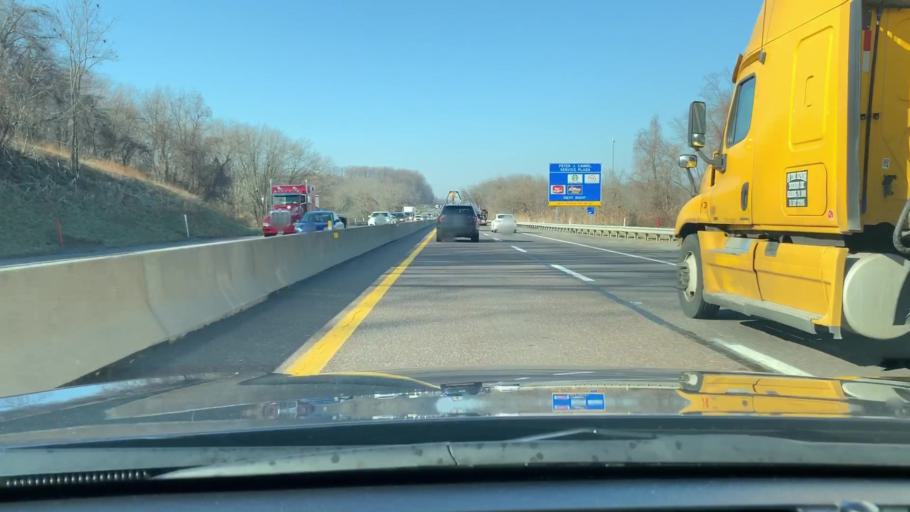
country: US
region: Pennsylvania
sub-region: Chester County
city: Elverson
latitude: 40.1177
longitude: -75.7680
